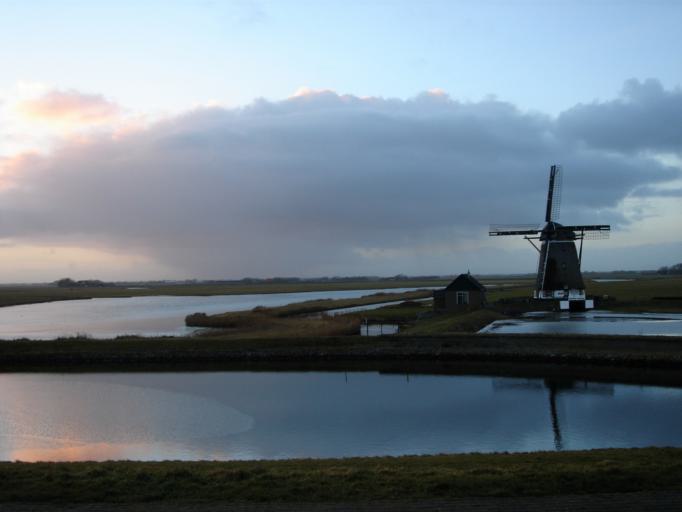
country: NL
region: North Holland
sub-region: Gemeente Texel
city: Den Burg
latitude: 53.1030
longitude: 4.8978
